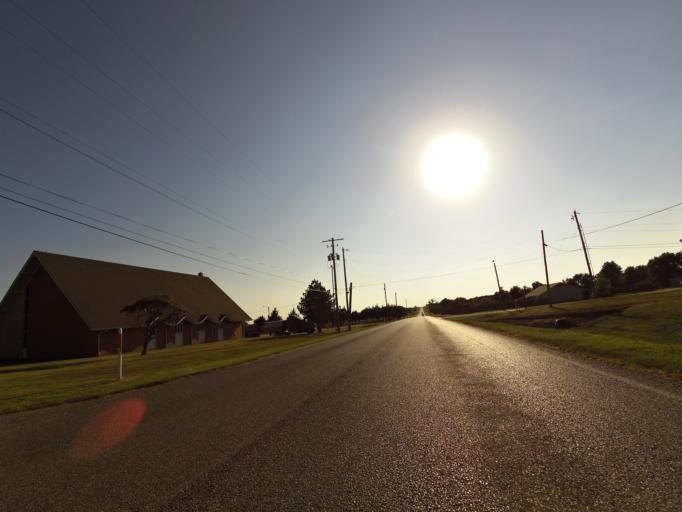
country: US
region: Kansas
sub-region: Reno County
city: Buhler
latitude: 38.1449
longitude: -97.7730
